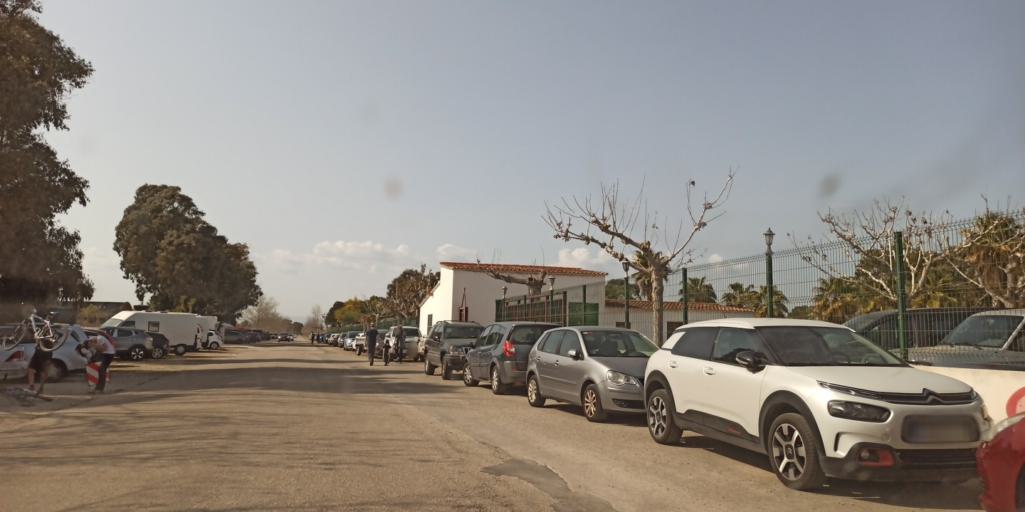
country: ES
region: Catalonia
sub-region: Provincia de Tarragona
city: Deltebre
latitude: 40.7200
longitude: 0.8487
